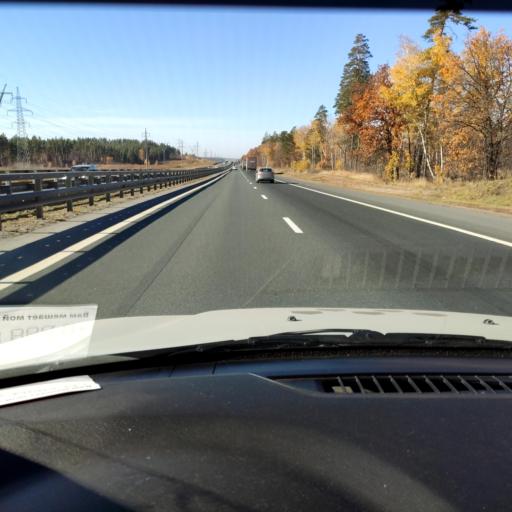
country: RU
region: Samara
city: Povolzhskiy
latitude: 53.5166
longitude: 49.7291
